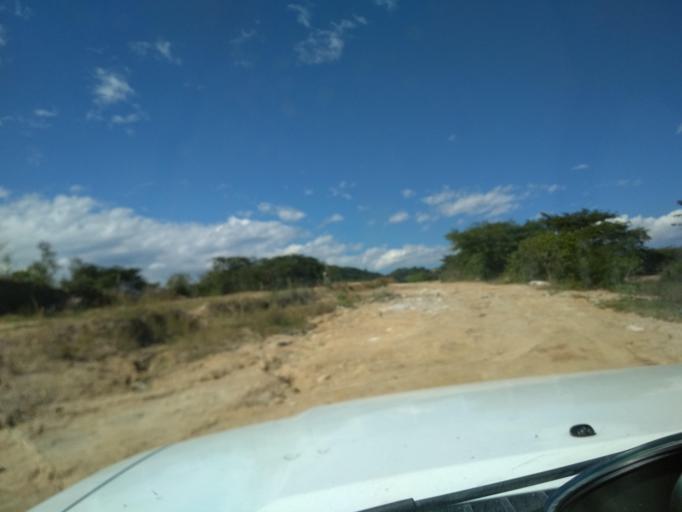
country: MX
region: Veracruz
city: El Castillo
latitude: 19.5470
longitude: -96.8543
